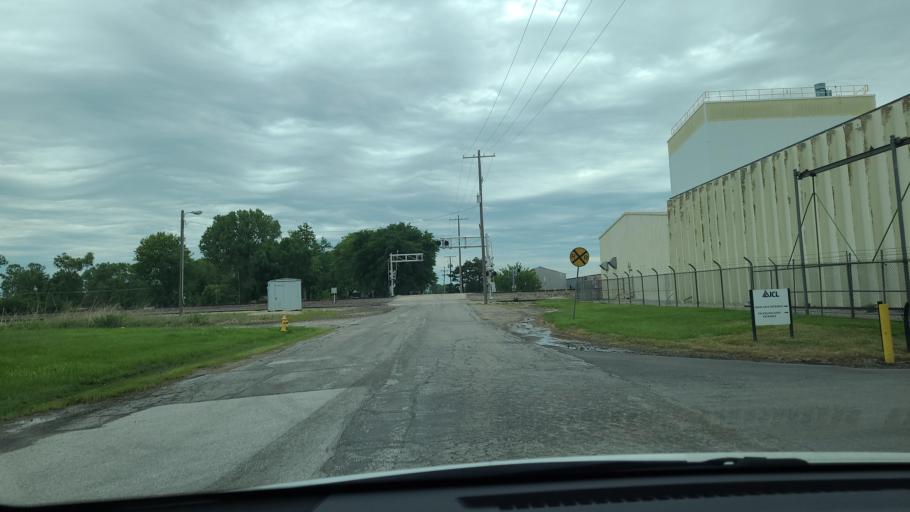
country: US
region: Kansas
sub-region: Douglas County
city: Lawrence
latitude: 38.9803
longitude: -95.2144
